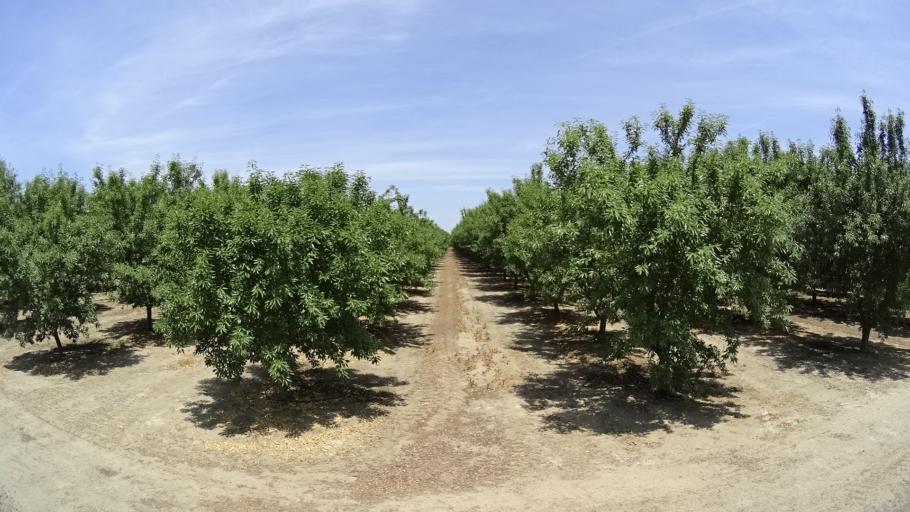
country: US
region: California
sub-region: Fresno County
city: Riverdale
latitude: 36.3875
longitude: -119.8754
